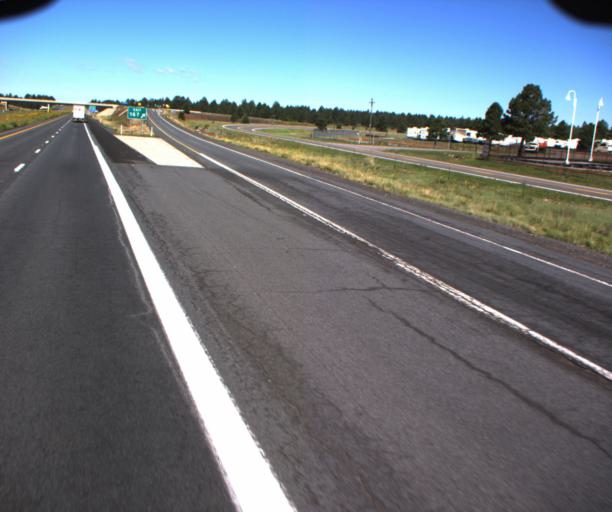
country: US
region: Arizona
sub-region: Coconino County
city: Williams
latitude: 35.2584
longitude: -112.1179
